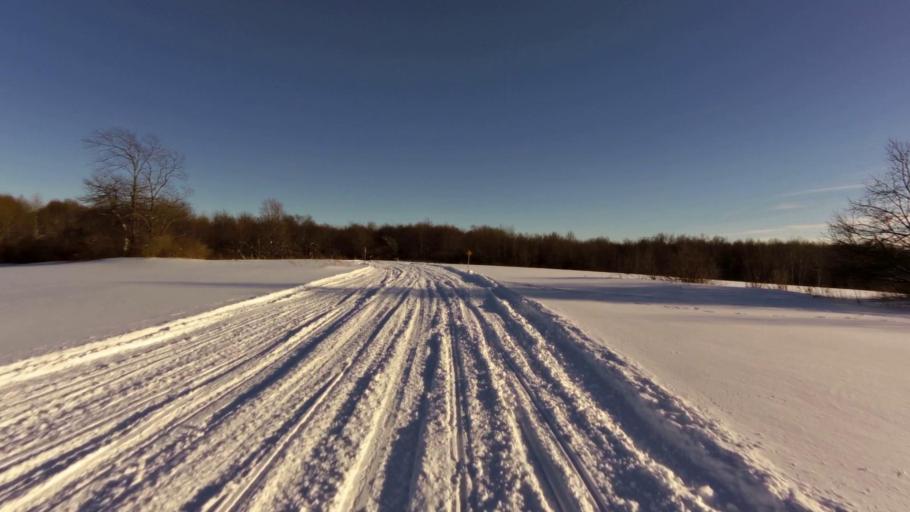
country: US
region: New York
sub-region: Chautauqua County
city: Mayville
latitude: 42.2379
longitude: -79.3916
